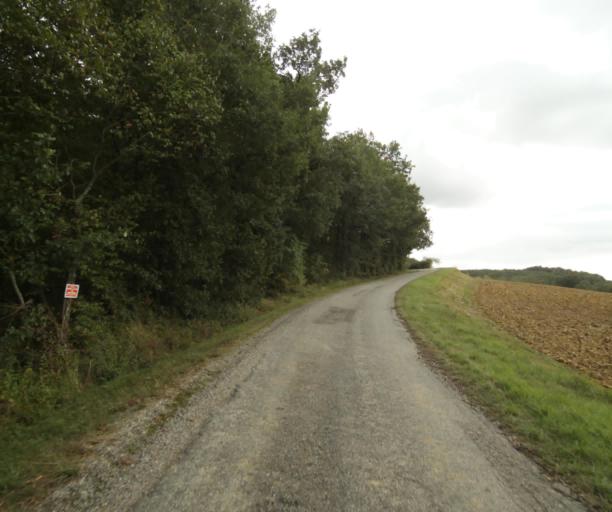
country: FR
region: Midi-Pyrenees
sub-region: Departement du Tarn-et-Garonne
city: Beaumont-de-Lomagne
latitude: 43.8911
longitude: 1.0807
